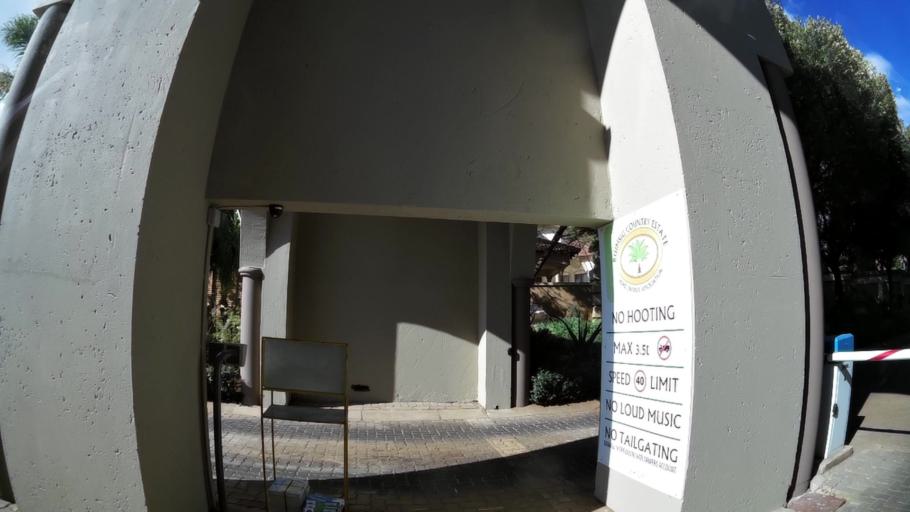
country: ZA
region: Gauteng
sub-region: West Rand District Municipality
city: Muldersdriseloop
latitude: -26.0699
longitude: 27.8494
